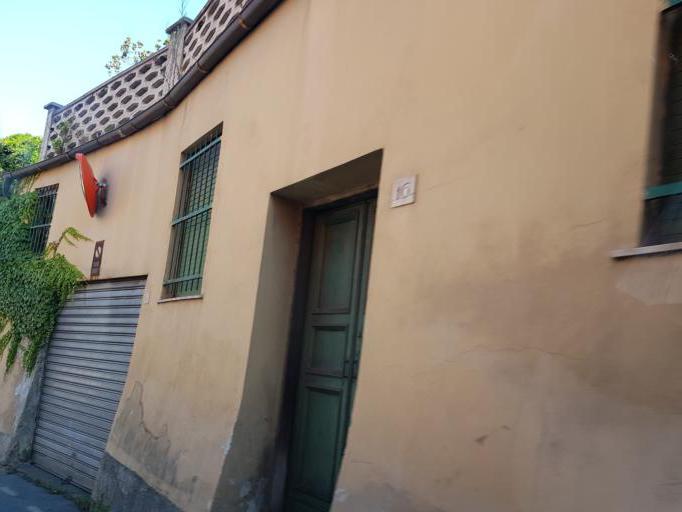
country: IT
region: Liguria
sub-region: Provincia di Genova
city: San Teodoro
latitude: 44.4175
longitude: 8.8757
